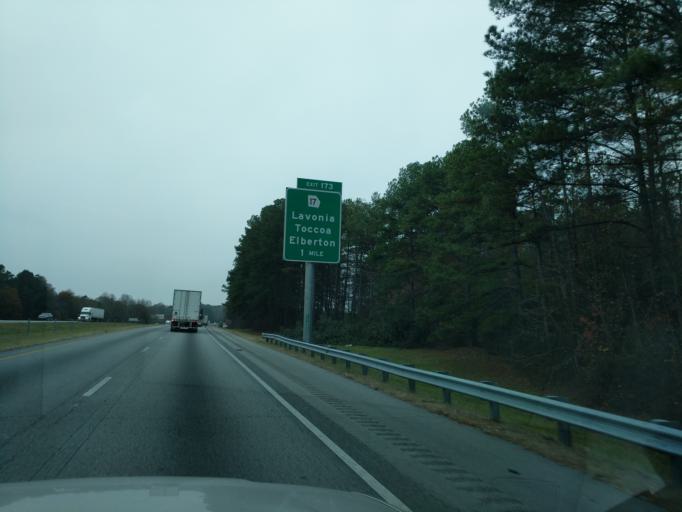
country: US
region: Georgia
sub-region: Franklin County
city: Lavonia
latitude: 34.4548
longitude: -83.1051
